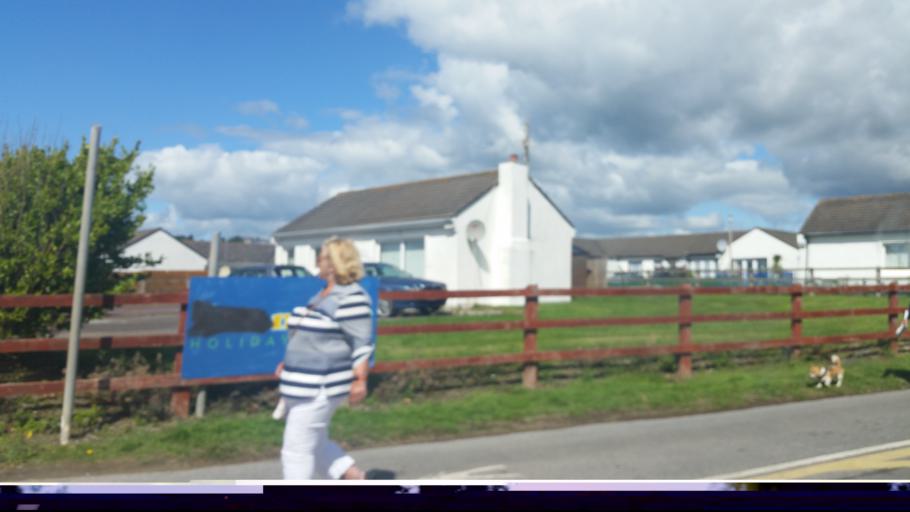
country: IE
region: Munster
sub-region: Waterford
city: Tra Mhor
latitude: 52.1629
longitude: -7.1399
